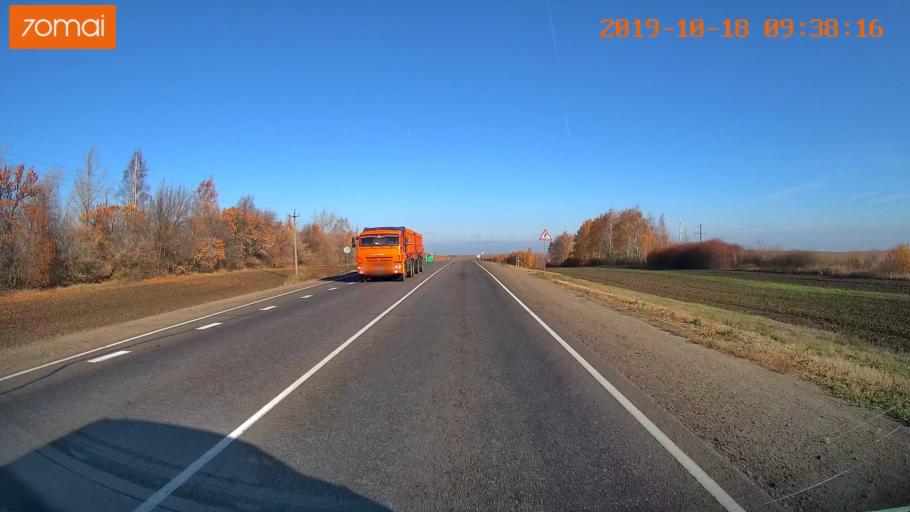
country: RU
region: Tula
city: Yefremov
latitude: 53.2353
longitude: 38.1377
